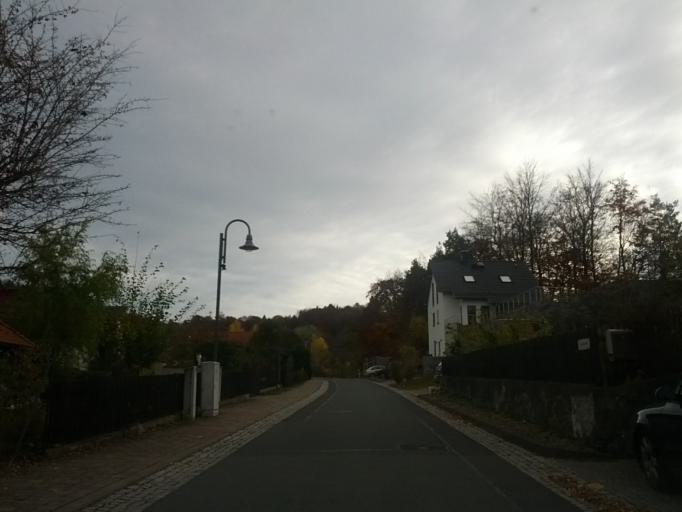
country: DE
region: Thuringia
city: Seebach
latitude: 50.9102
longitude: 10.4334
